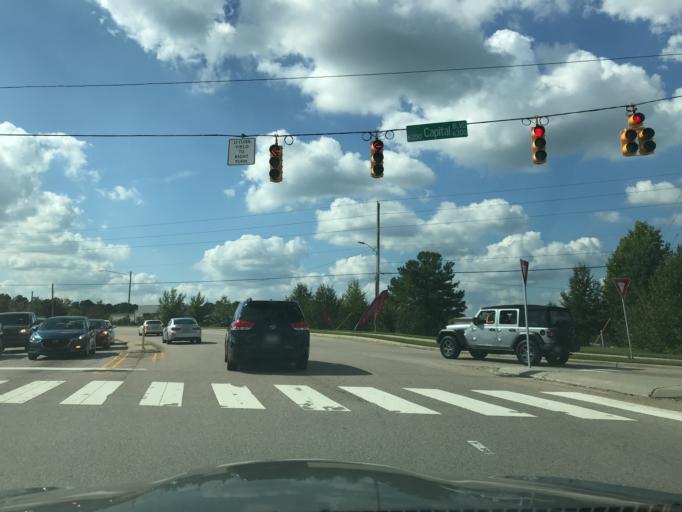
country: US
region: North Carolina
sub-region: Wake County
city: Raleigh
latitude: 35.8709
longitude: -78.5806
